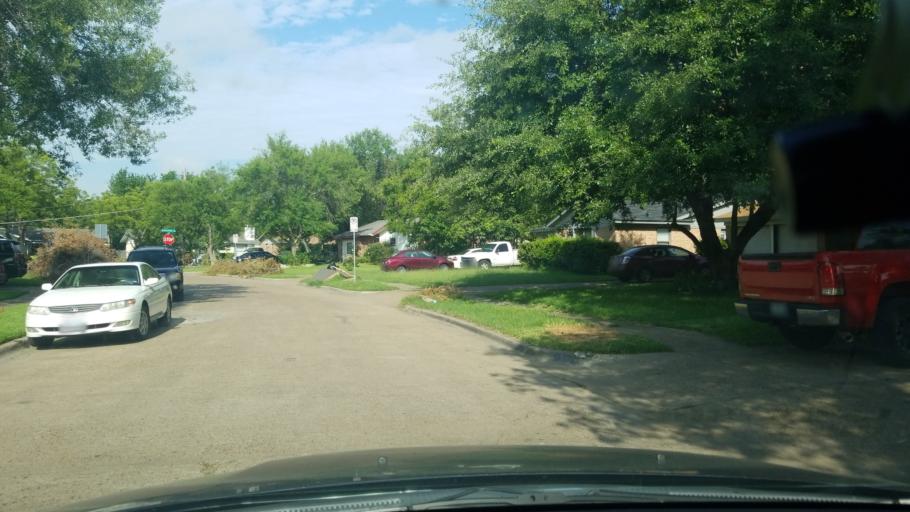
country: US
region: Texas
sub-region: Dallas County
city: Balch Springs
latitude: 32.7469
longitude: -96.6708
